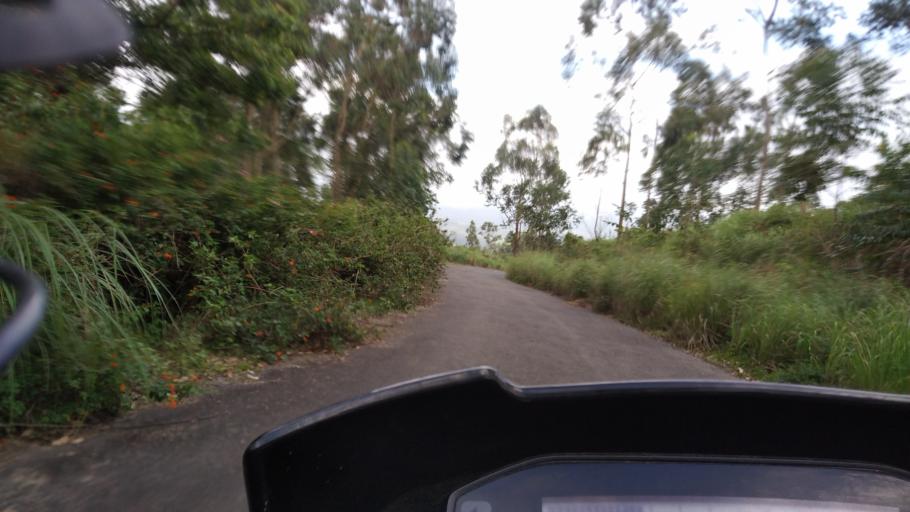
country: IN
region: Kerala
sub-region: Idukki
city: Munnar
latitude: 10.0404
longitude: 77.1828
